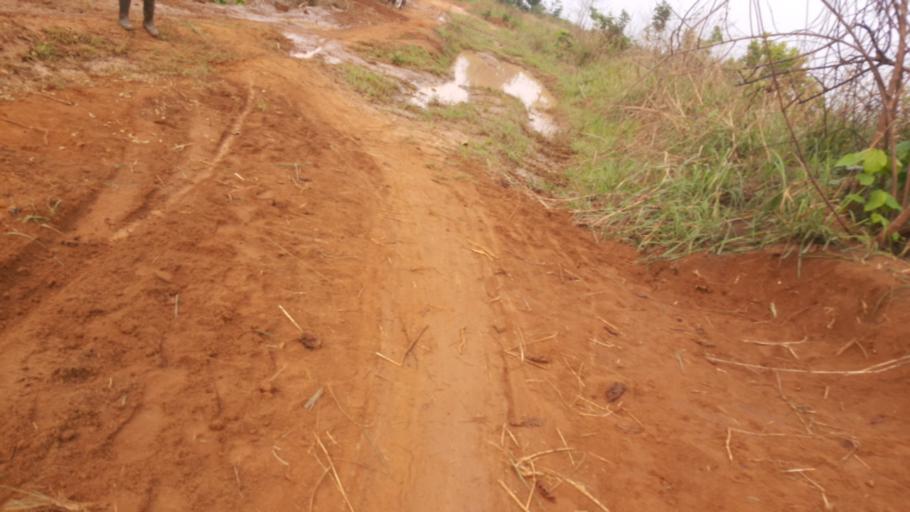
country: CD
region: Bandundu
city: Bandundu
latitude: -3.4634
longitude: 17.7168
